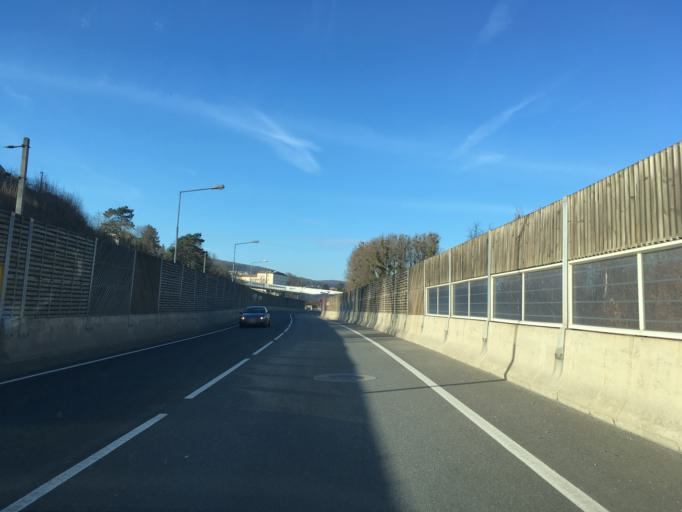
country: AT
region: Lower Austria
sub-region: Politischer Bezirk Wien-Umgebung
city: Klosterneuburg
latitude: 48.3141
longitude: 16.3209
